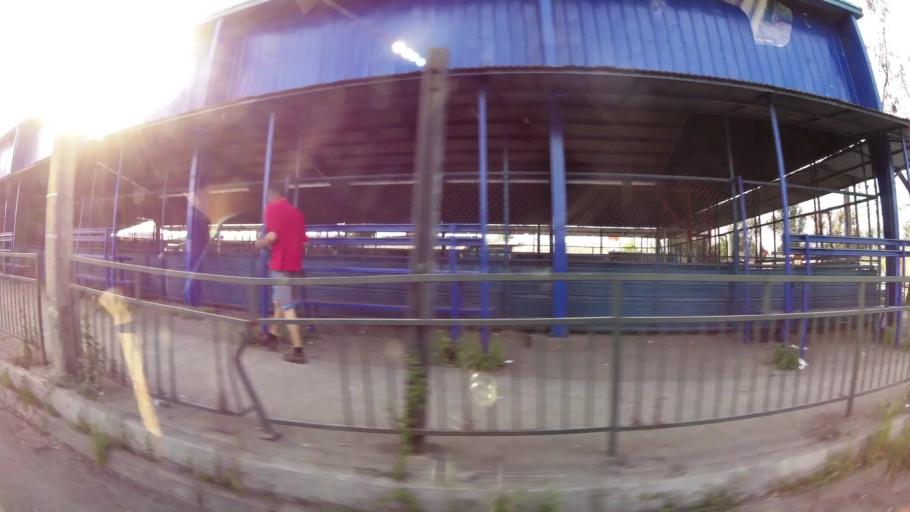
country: CL
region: Santiago Metropolitan
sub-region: Provincia de Cordillera
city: Puente Alto
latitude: -33.6174
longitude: -70.5691
